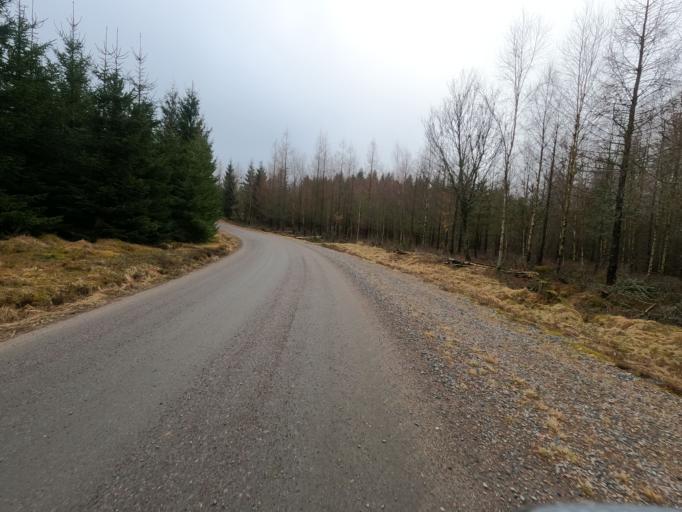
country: SE
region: Kronoberg
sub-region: Markaryds Kommun
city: Stromsnasbruk
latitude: 56.8137
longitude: 13.5698
